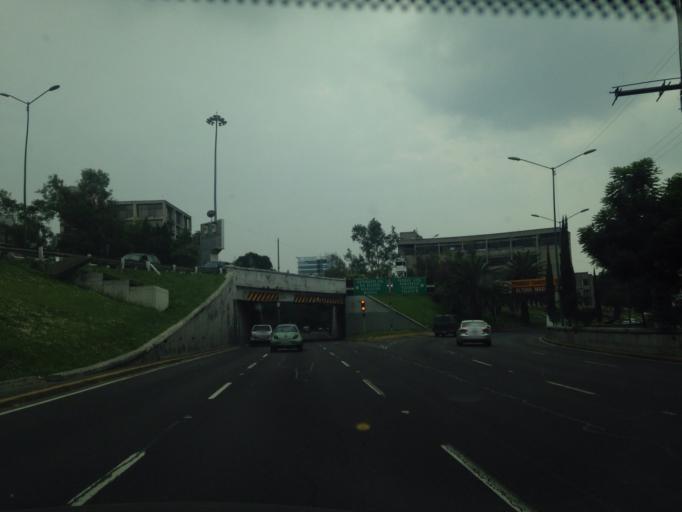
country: MX
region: Mexico City
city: Benito Juarez
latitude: 19.3985
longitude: -99.1748
